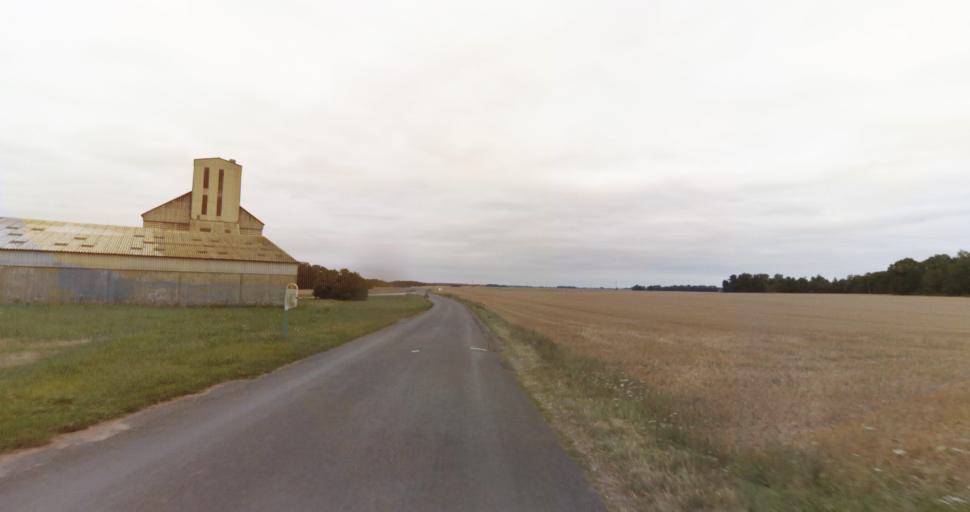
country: FR
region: Haute-Normandie
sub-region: Departement de l'Eure
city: Saint-Germain-sur-Avre
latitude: 48.7998
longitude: 1.2761
